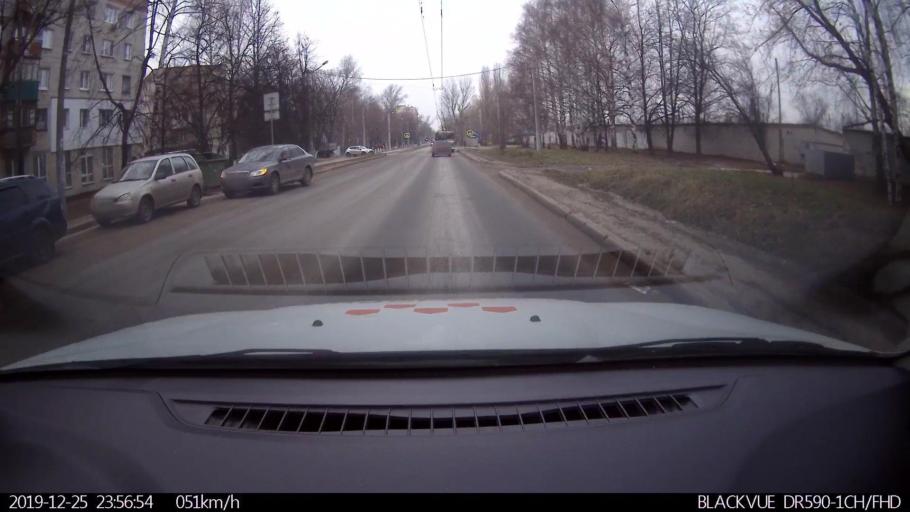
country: RU
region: Nizjnij Novgorod
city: Gorbatovka
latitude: 56.2588
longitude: 43.8669
